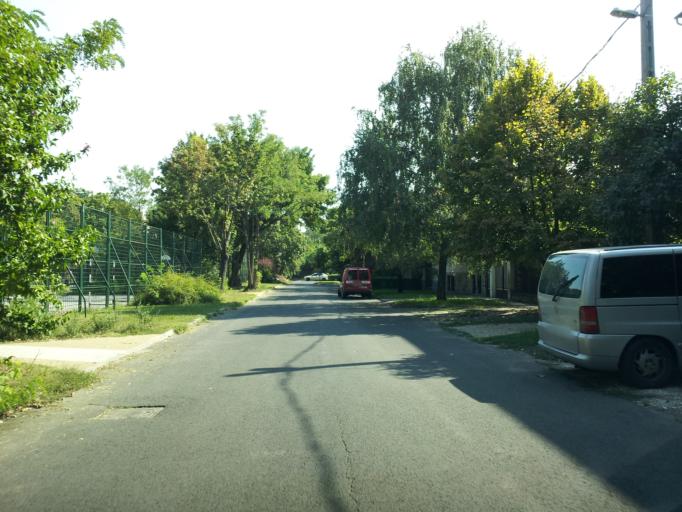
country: HU
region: Budapest
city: Budapest XIV. keruelet
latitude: 47.5113
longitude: 19.1078
